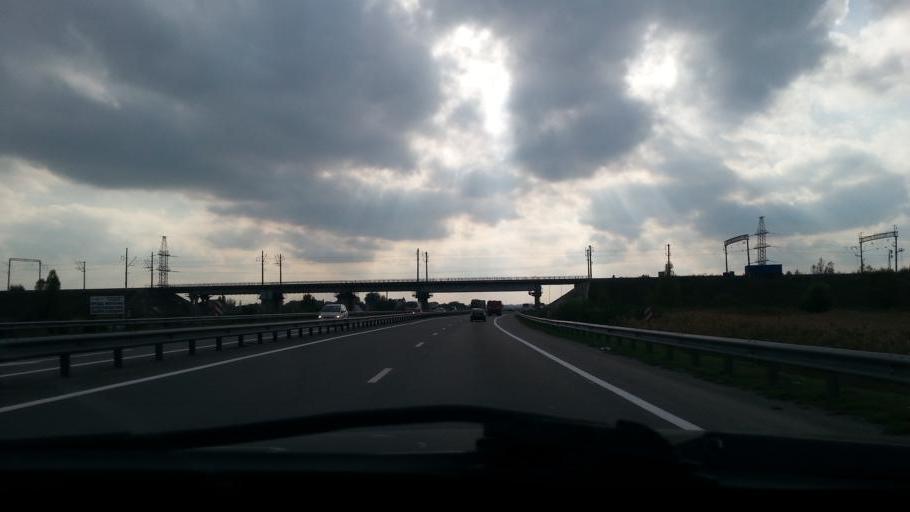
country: RU
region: Rostov
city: Bataysk
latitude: 47.1453
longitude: 39.7008
